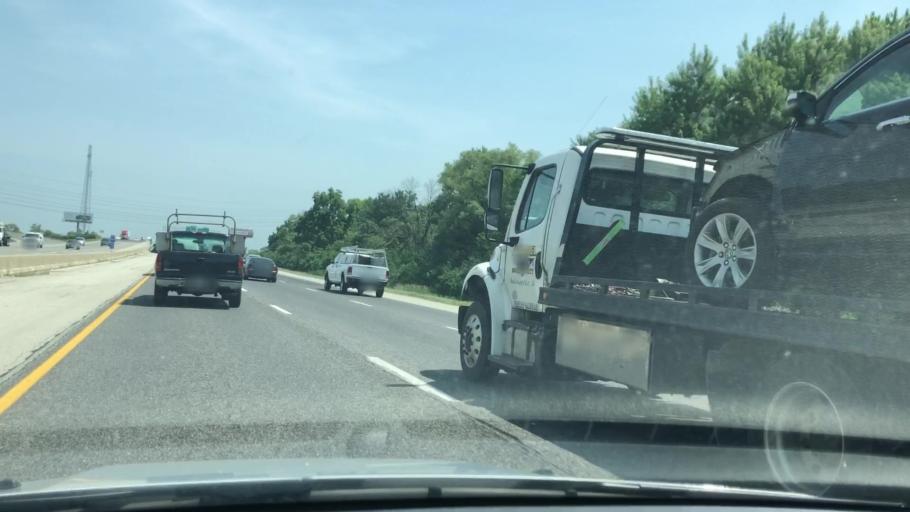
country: US
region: Indiana
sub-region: Marion County
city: Lawrence
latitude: 39.8997
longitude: -86.0617
